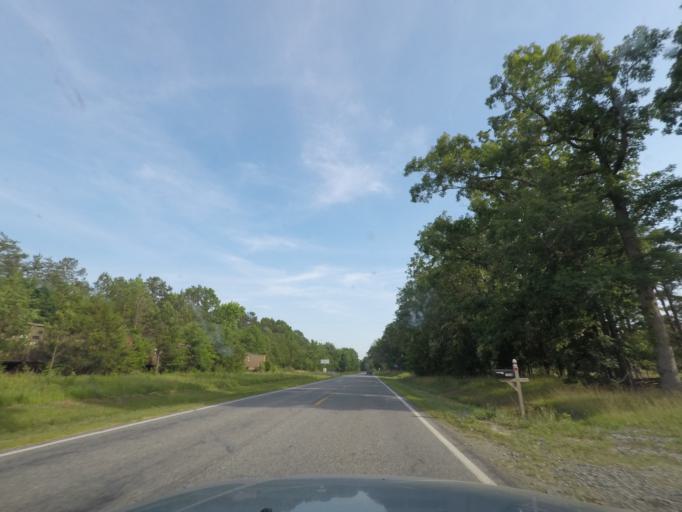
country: US
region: Virginia
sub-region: Mecklenburg County
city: Clarksville
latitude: 36.5428
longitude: -78.5394
